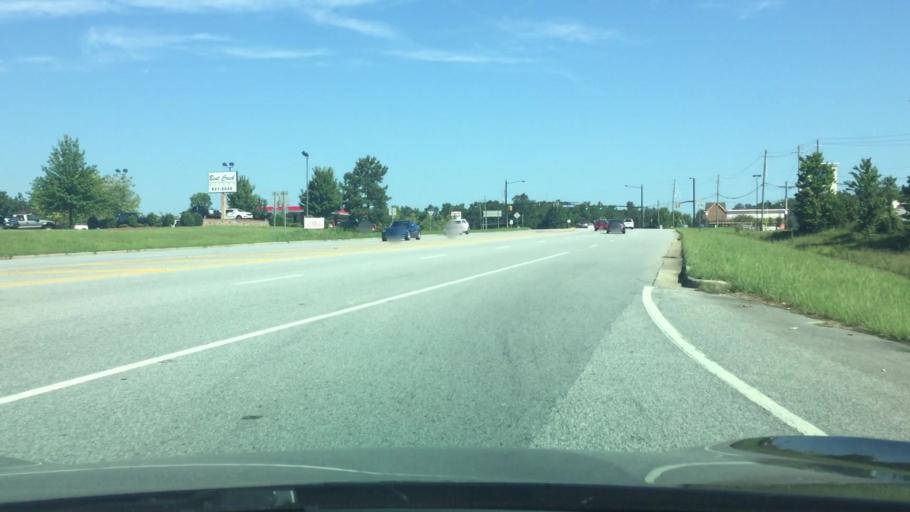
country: US
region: Alabama
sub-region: Lee County
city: Auburn
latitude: 32.6061
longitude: -85.4290
